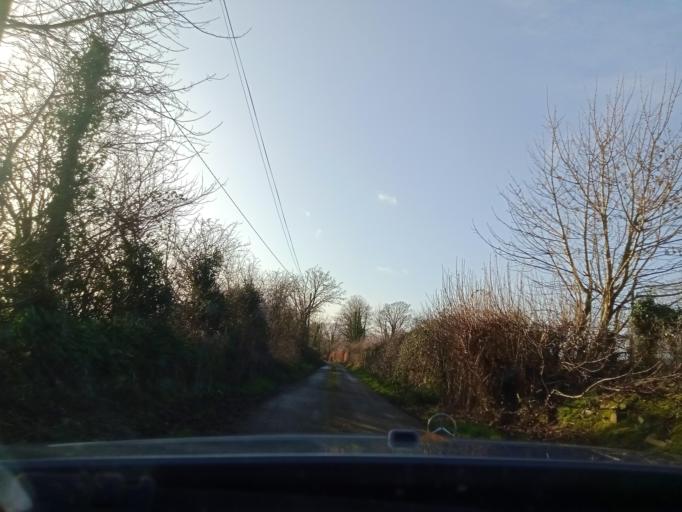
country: IE
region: Leinster
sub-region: Kilkenny
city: Callan
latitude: 52.4883
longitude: -7.4000
